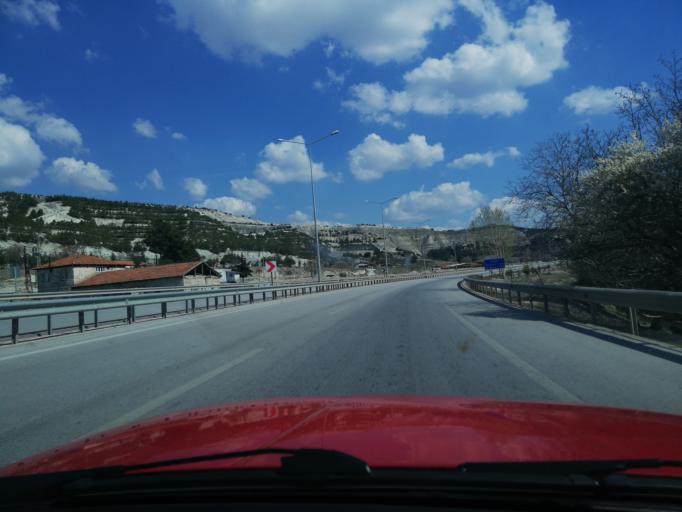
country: TR
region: Burdur
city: Burdur
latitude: 37.7086
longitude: 30.3033
